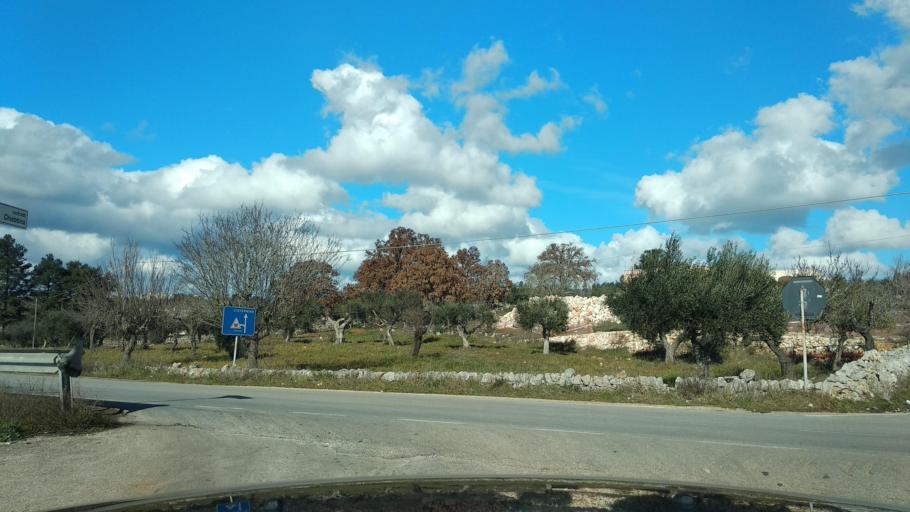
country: IT
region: Apulia
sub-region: Provincia di Brindisi
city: Cisternino
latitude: 40.7232
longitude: 17.4454
